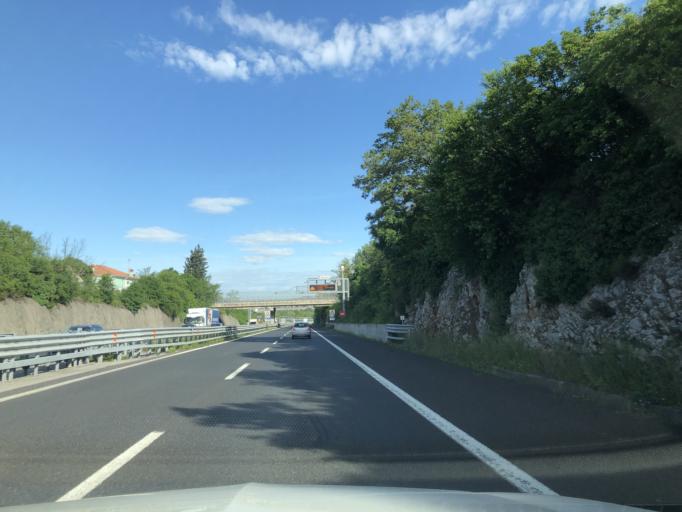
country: IT
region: Friuli Venezia Giulia
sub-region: Provincia di Trieste
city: Aurisina
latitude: 45.7474
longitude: 13.6835
